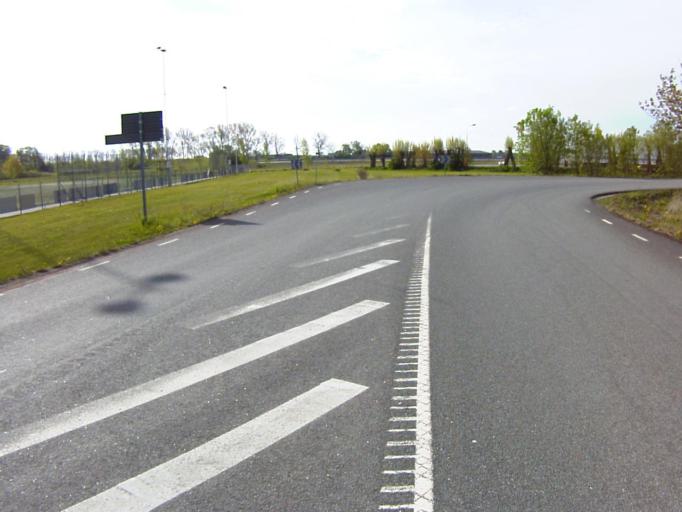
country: SE
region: Skane
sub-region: Kristianstads Kommun
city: Fjalkinge
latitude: 56.0363
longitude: 14.2690
